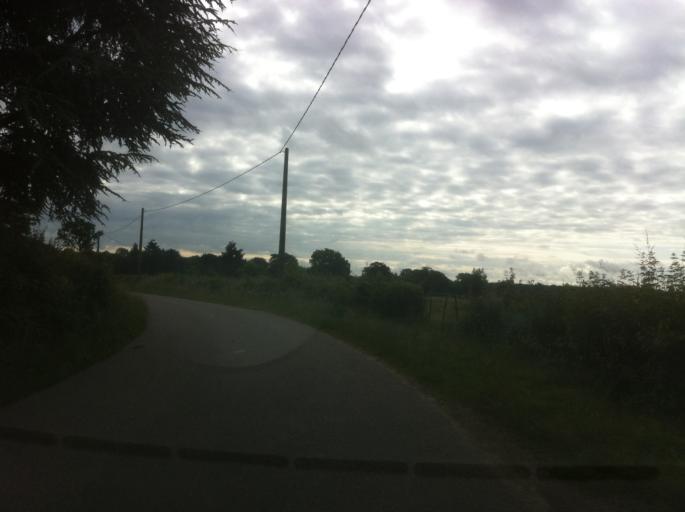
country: FR
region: Auvergne
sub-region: Departement de l'Allier
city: Montmarault
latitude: 46.3292
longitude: 3.0682
